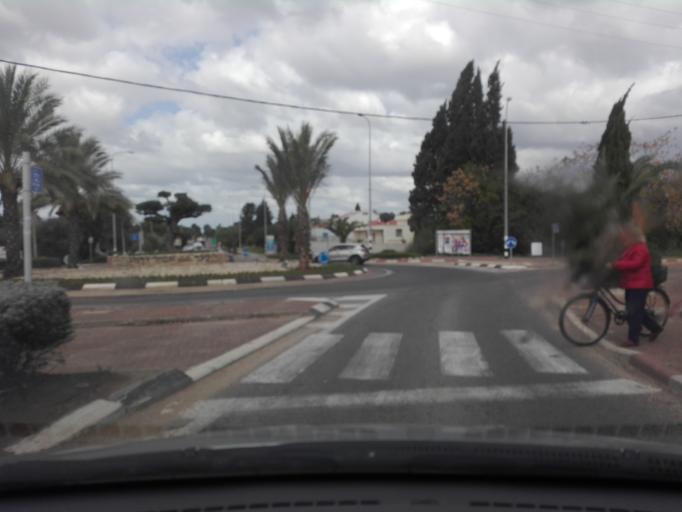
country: IL
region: Haifa
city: Hadera
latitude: 32.4721
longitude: 34.9787
